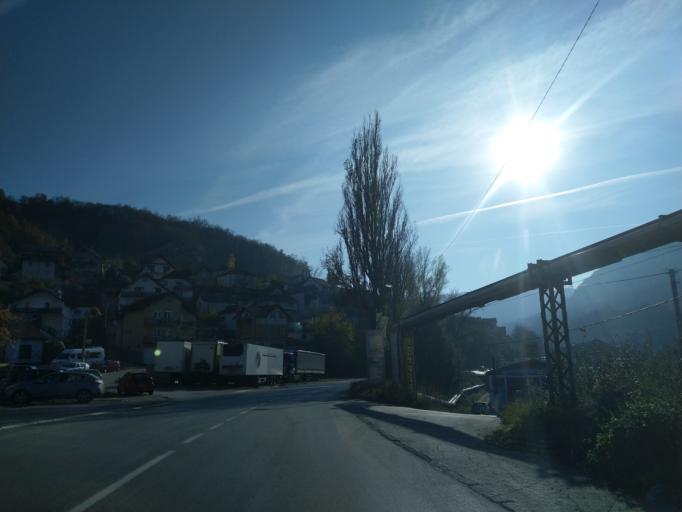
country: RS
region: Central Serbia
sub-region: Zlatiborski Okrug
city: Uzice
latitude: 43.8461
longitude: 19.8633
